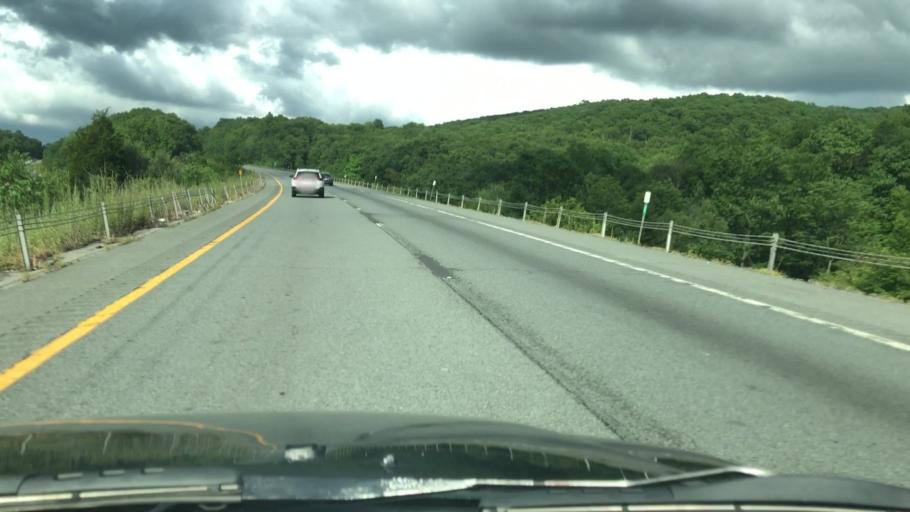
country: US
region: New York
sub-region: Orange County
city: Port Jervis
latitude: 41.3585
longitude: -74.6638
